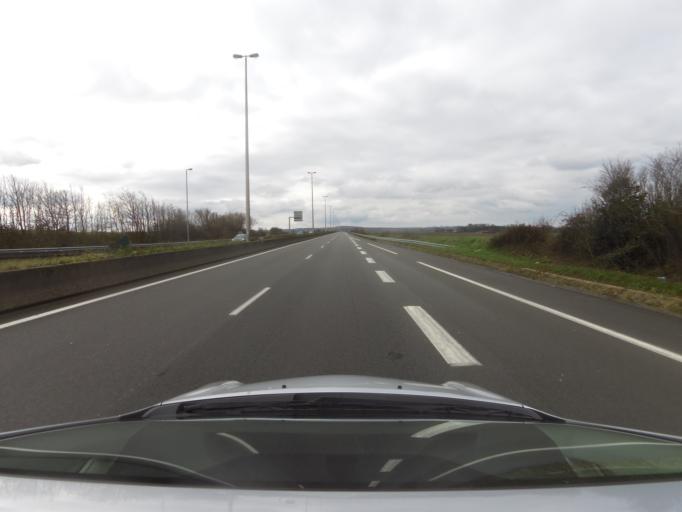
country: FR
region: Nord-Pas-de-Calais
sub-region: Departement du Pas-de-Calais
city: Marquise
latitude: 50.8258
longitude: 1.6997
